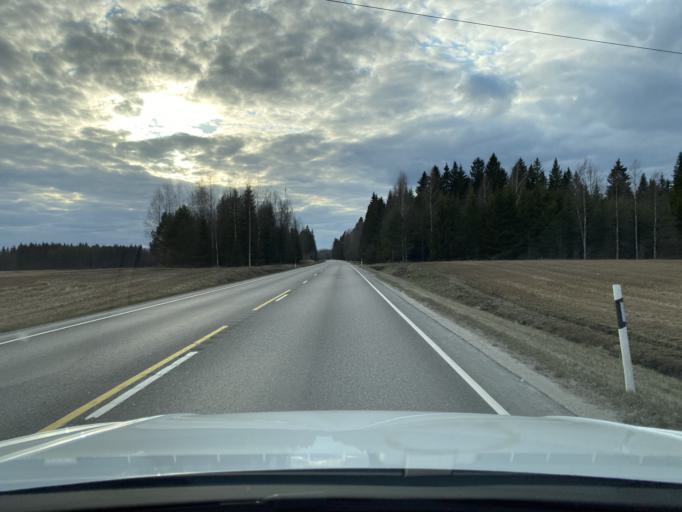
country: FI
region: Haeme
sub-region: Haemeenlinna
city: Renko
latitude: 60.7845
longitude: 24.1488
